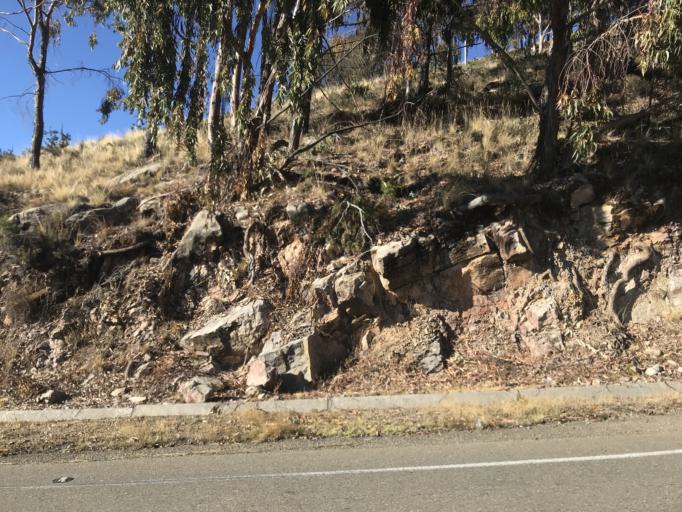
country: BO
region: La Paz
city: San Pedro
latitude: -16.2266
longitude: -68.8530
